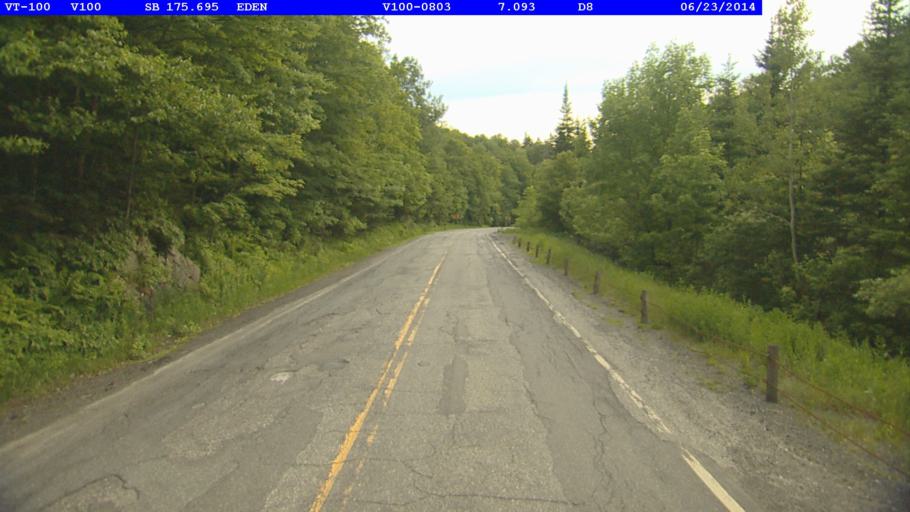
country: US
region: Vermont
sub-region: Lamoille County
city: Hyde Park
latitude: 44.7332
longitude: -72.4730
